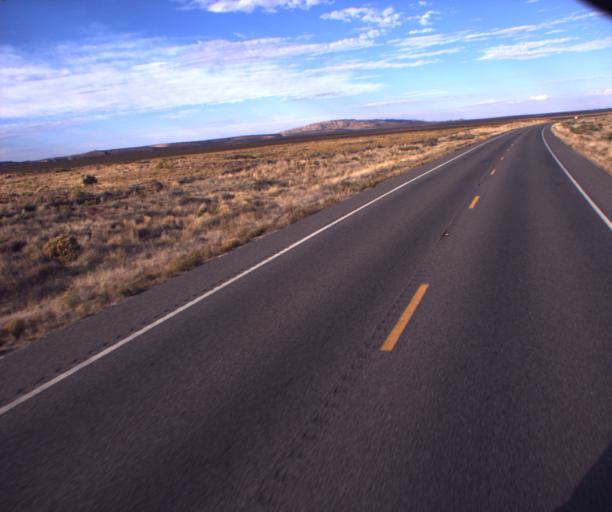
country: US
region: Arizona
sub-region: Apache County
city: Lukachukai
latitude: 36.9297
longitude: -109.2133
